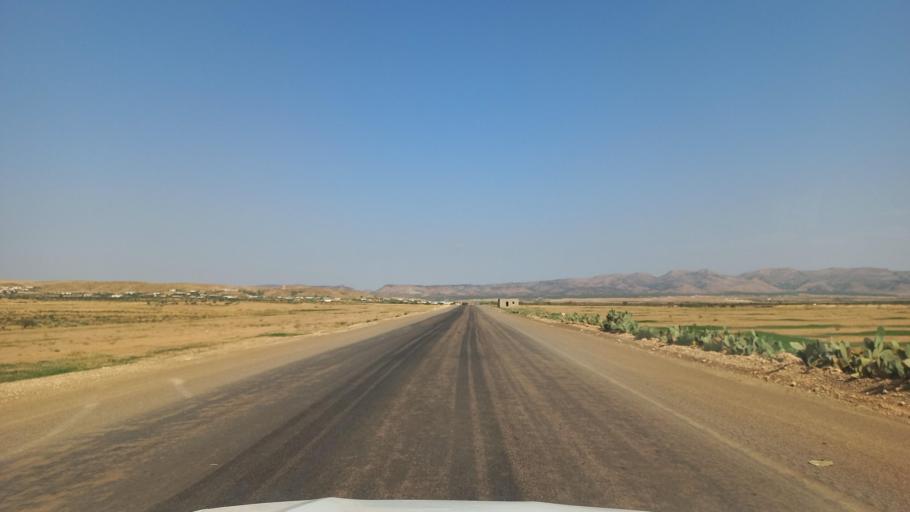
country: TN
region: Al Qasrayn
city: Sbiba
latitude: 35.3705
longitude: 9.0371
